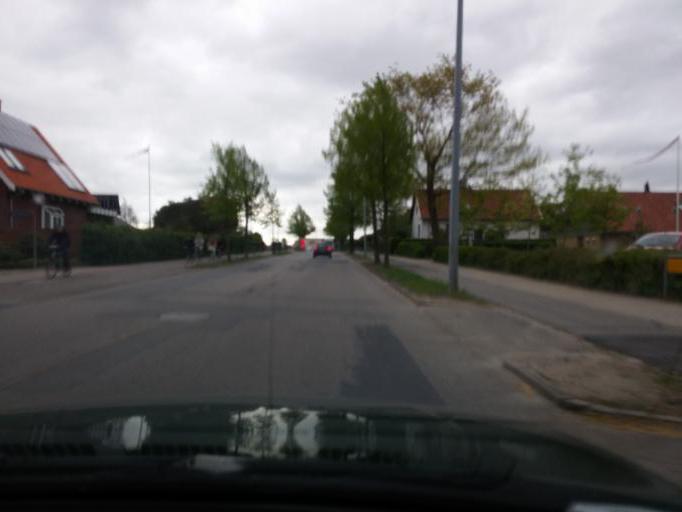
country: DK
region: South Denmark
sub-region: Odense Kommune
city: Odense
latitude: 55.3856
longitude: 10.4171
